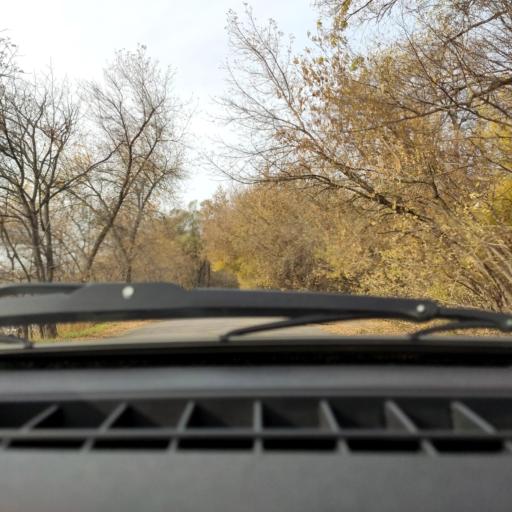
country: RU
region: Bashkortostan
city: Ufa
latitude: 54.7847
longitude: 56.1667
